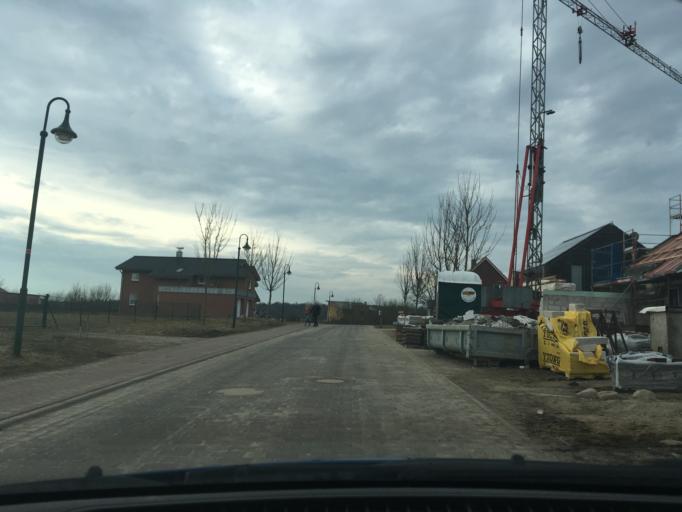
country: DE
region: Mecklenburg-Vorpommern
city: Zarrentin
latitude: 53.5602
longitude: 10.9107
